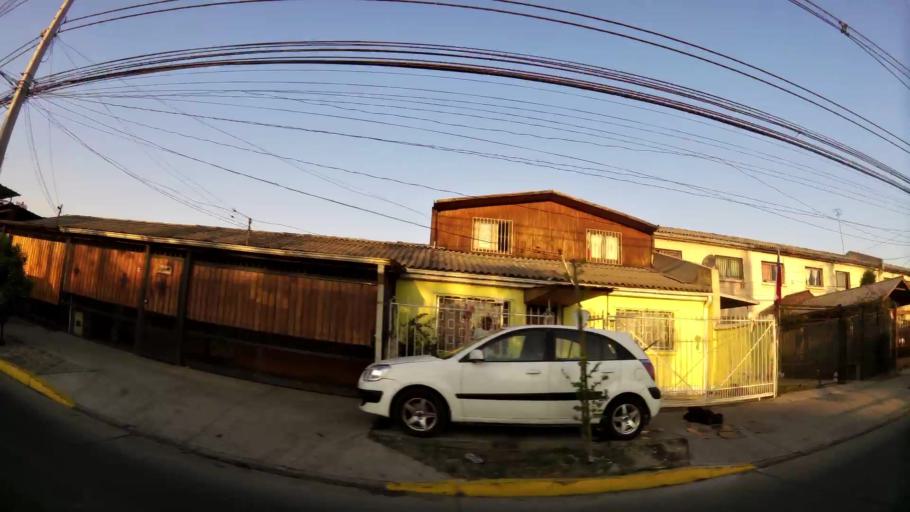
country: CL
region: Santiago Metropolitan
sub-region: Provincia de Santiago
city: Santiago
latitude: -33.5000
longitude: -70.6391
